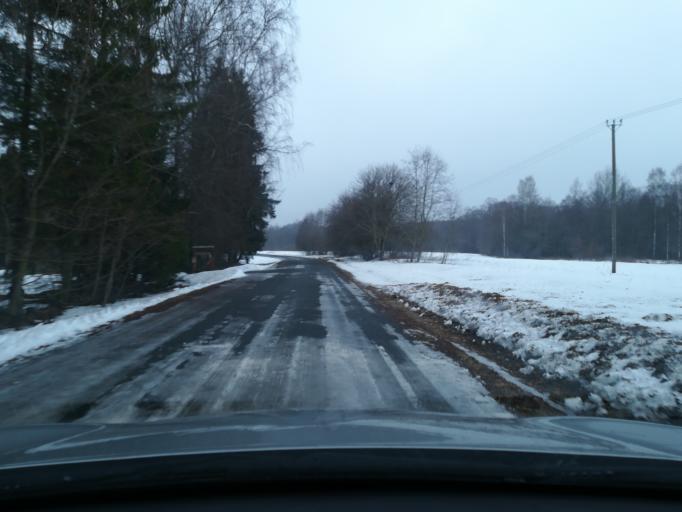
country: EE
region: Harju
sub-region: Loksa linn
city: Loksa
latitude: 59.4670
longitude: 25.7020
